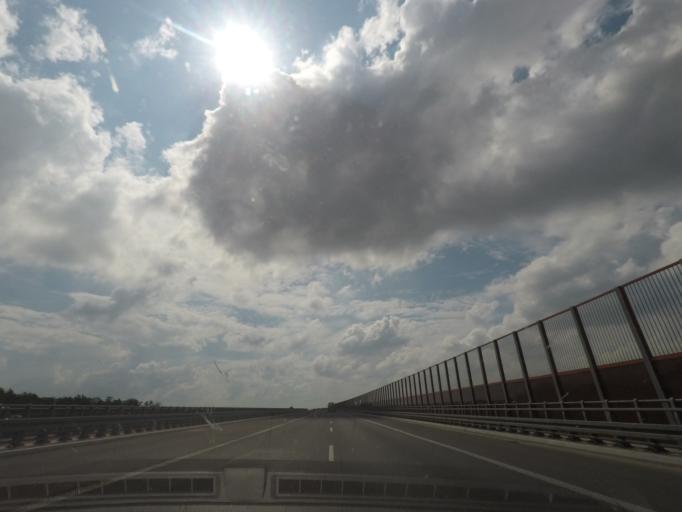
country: PL
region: Lodz Voivodeship
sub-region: Powiat kutnowski
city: Krzyzanow
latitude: 52.1397
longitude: 19.4835
